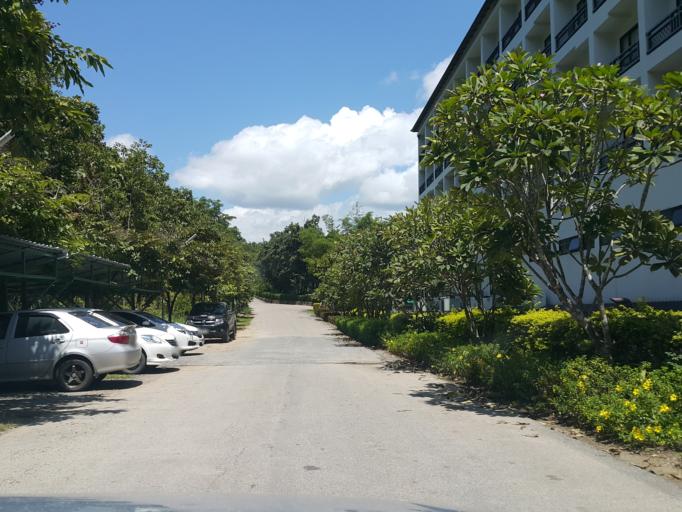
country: TH
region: Chiang Mai
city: San Kamphaeng
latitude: 18.6921
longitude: 99.1733
